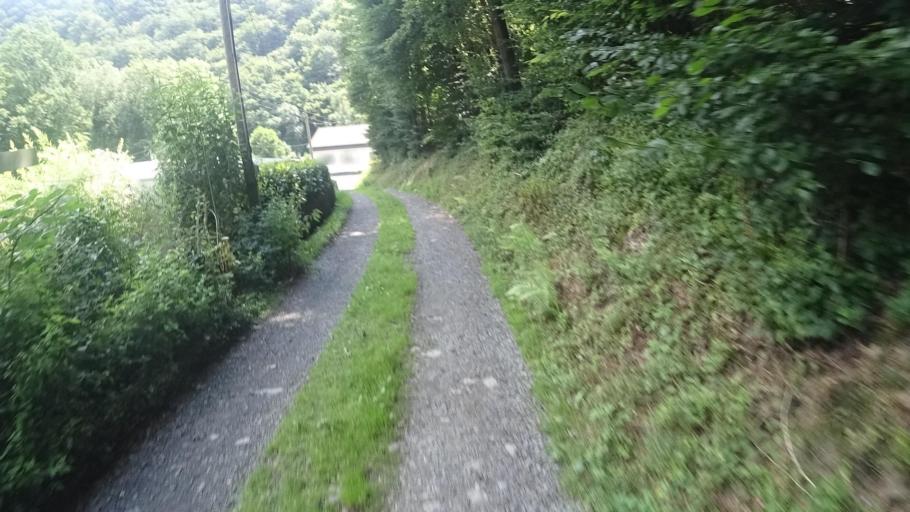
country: DE
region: Rheinland-Pfalz
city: Sankt Katharinen
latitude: 50.5849
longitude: 7.3919
